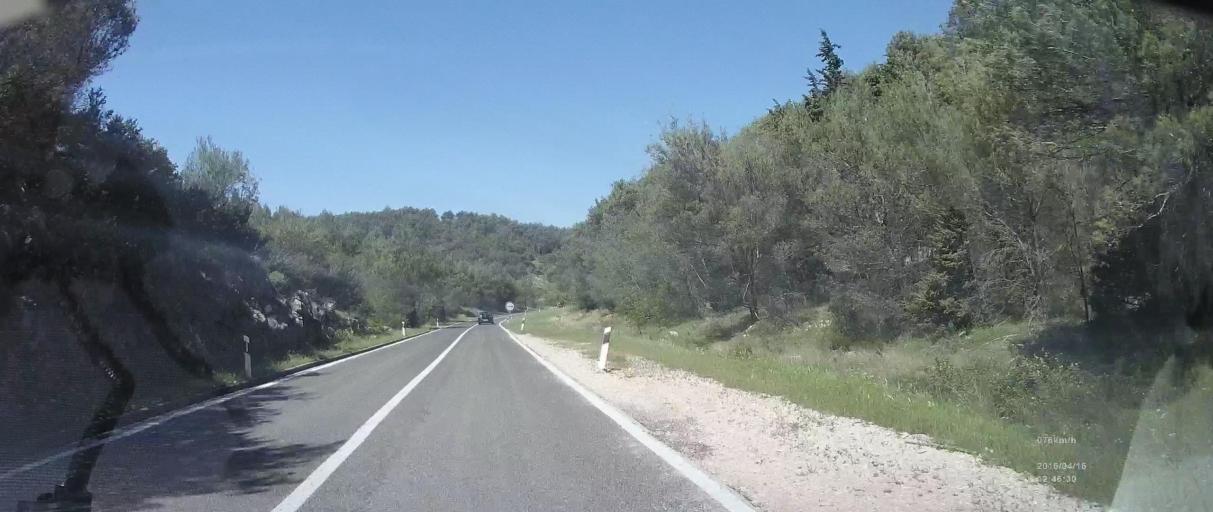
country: HR
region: Sibensko-Kniniska
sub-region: Grad Sibenik
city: Brodarica
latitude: 43.6556
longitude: 16.0534
